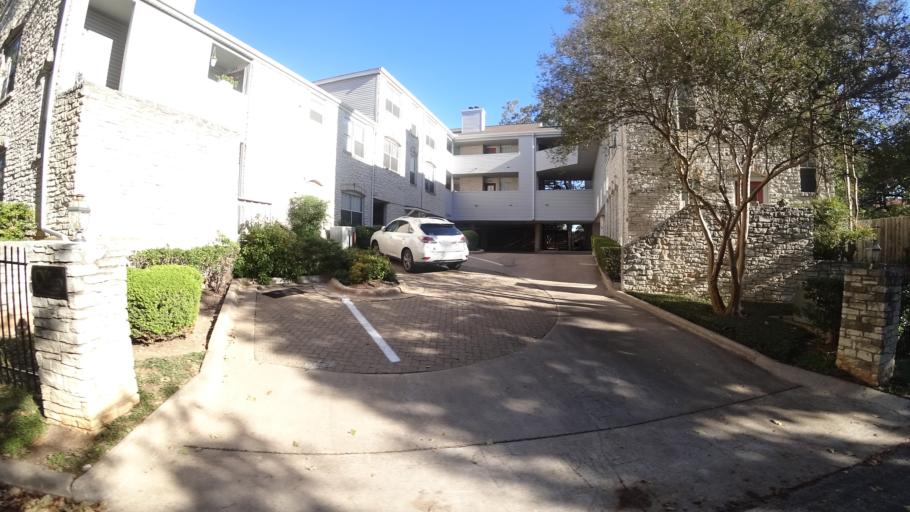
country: US
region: Texas
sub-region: Travis County
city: Rollingwood
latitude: 30.2878
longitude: -97.7721
